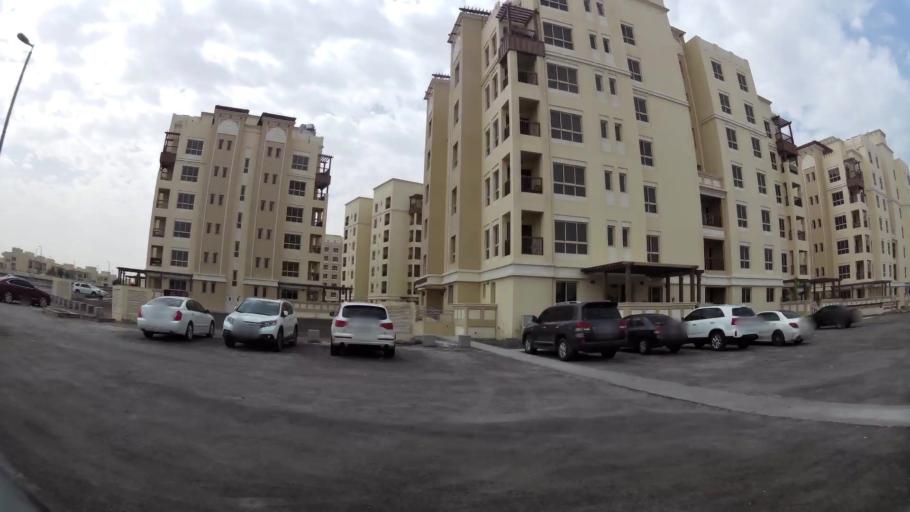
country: AE
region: Abu Dhabi
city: Abu Dhabi
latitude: 24.3134
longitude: 54.6236
